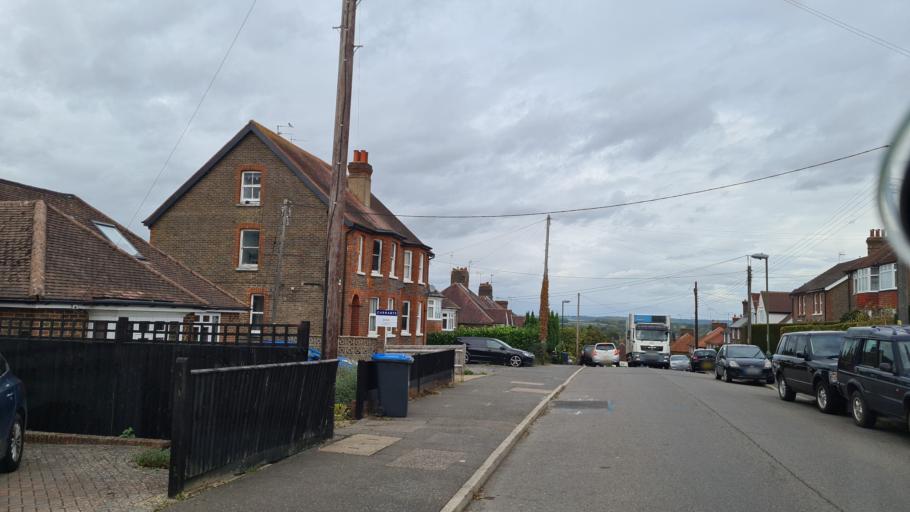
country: GB
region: England
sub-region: West Sussex
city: Haywards Heath
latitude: 50.9969
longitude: -0.0933
